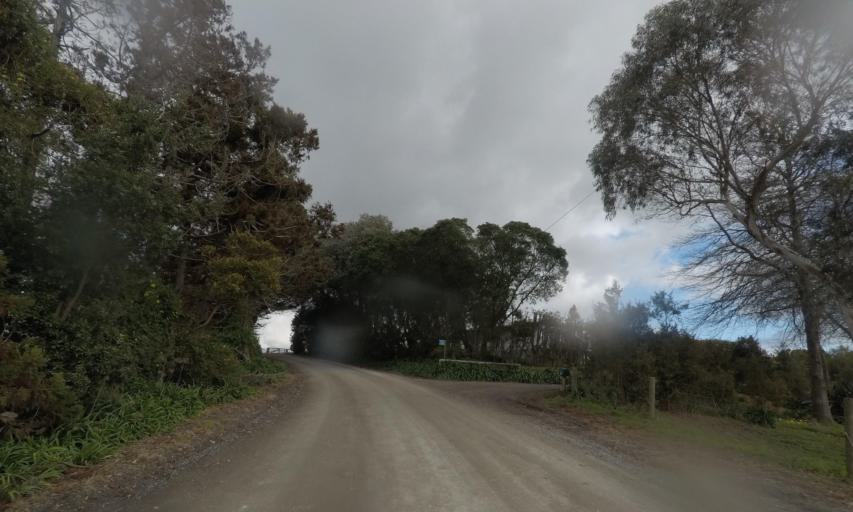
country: NZ
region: Auckland
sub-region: Auckland
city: Wellsford
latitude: -36.1622
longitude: 174.6034
